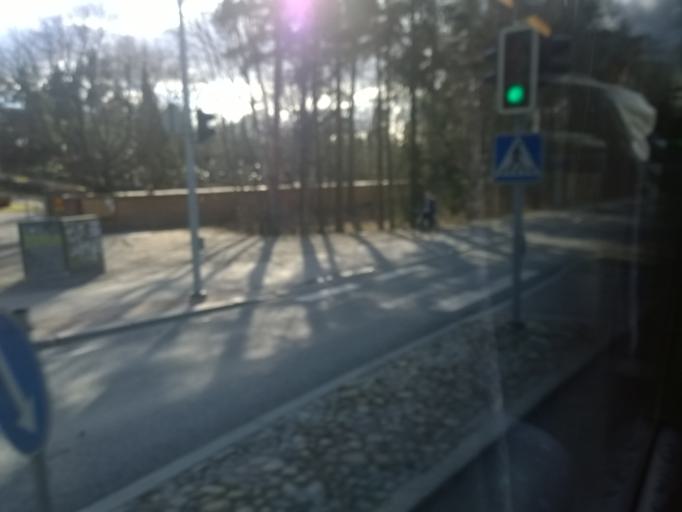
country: FI
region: Pirkanmaa
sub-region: Tampere
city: Tampere
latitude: 61.4943
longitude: 23.8004
